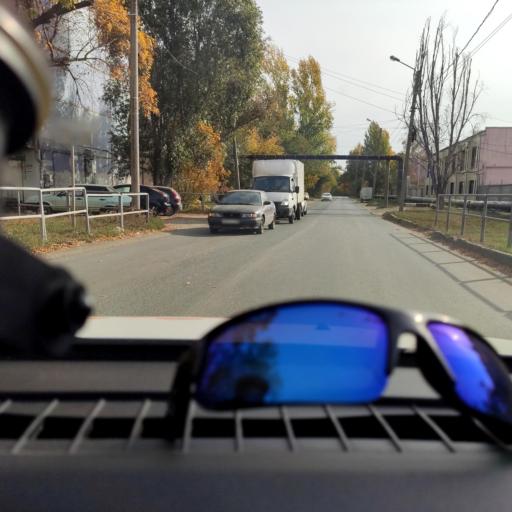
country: RU
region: Samara
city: Samara
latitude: 53.1198
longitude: 50.0870
